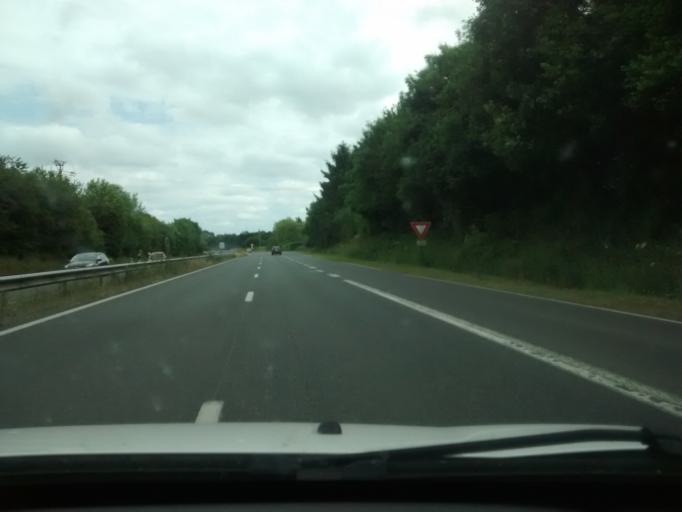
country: FR
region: Brittany
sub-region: Departement des Cotes-d'Armor
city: Cavan
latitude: 48.6570
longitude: -3.3366
